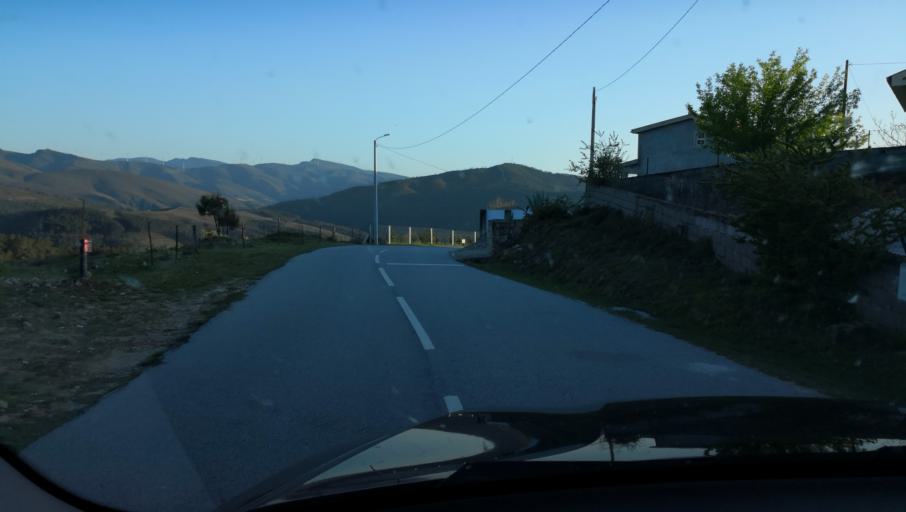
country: PT
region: Vila Real
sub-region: Mondim de Basto
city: Mondim de Basto
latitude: 41.4117
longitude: -7.8749
